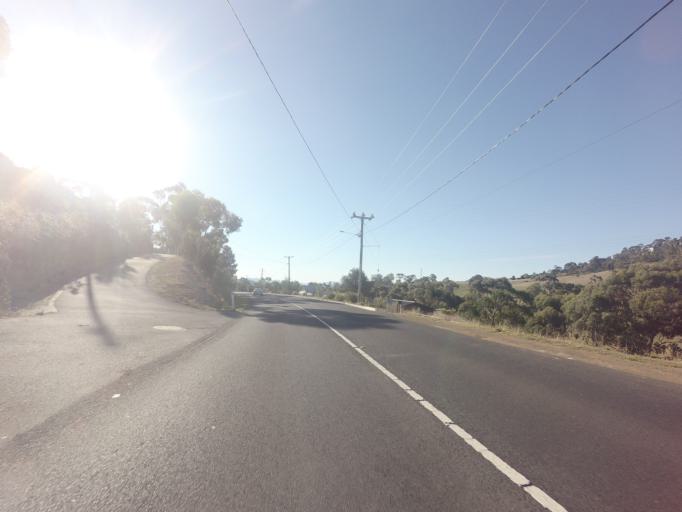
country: AU
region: Tasmania
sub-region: Glenorchy
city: West Moonah
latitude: -42.8570
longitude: 147.2691
